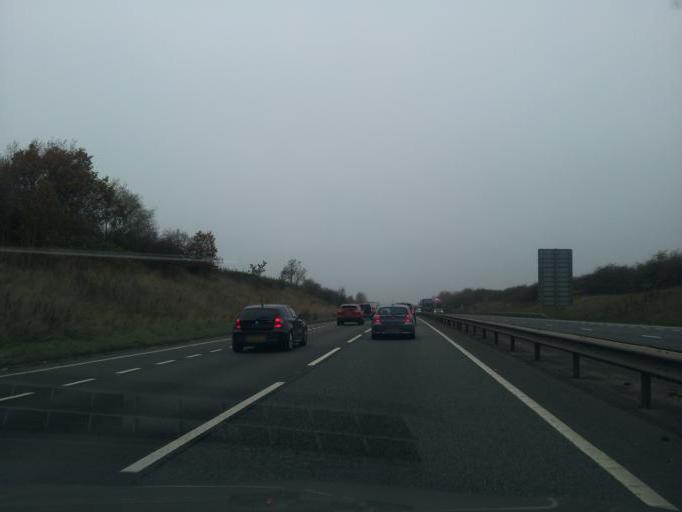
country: GB
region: England
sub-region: Leicestershire
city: Glenfield
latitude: 52.6590
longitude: -1.2110
